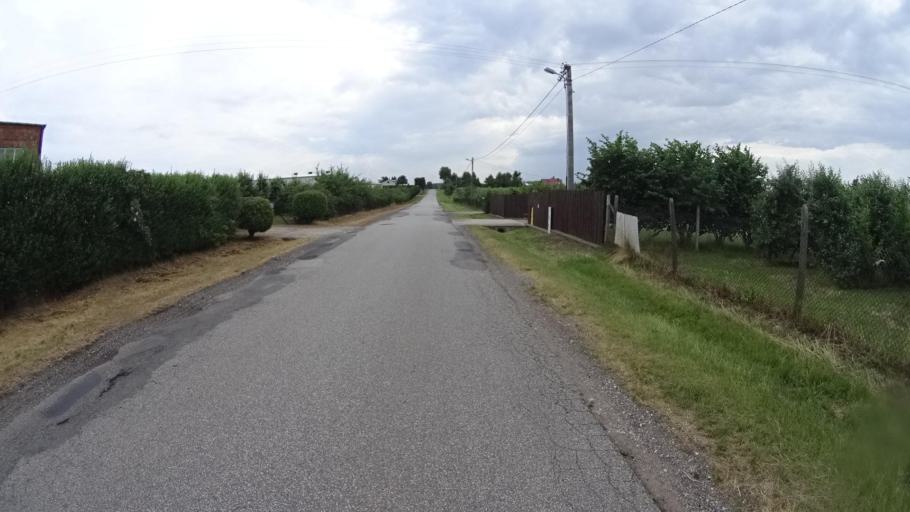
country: PL
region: Masovian Voivodeship
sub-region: Powiat grojecki
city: Belsk Duzy
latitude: 51.7963
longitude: 20.8584
